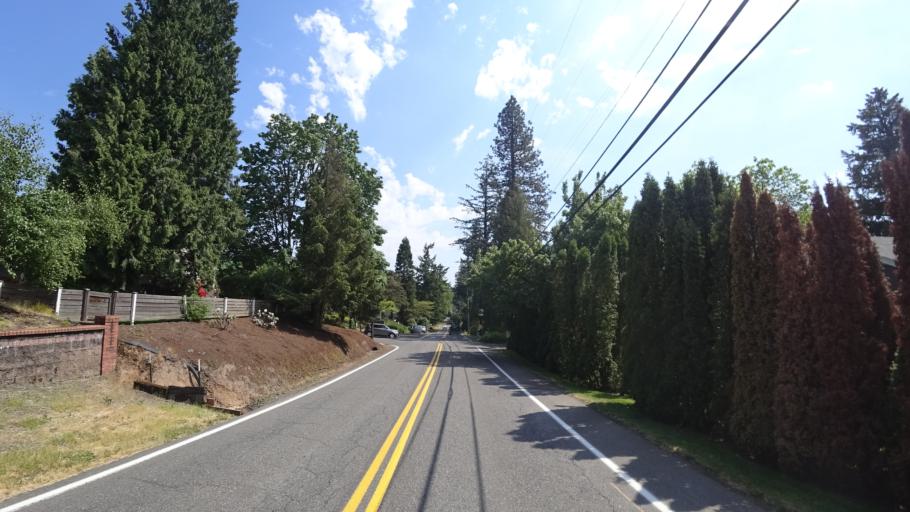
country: US
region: Oregon
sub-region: Multnomah County
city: Portland
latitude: 45.4891
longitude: -122.7104
